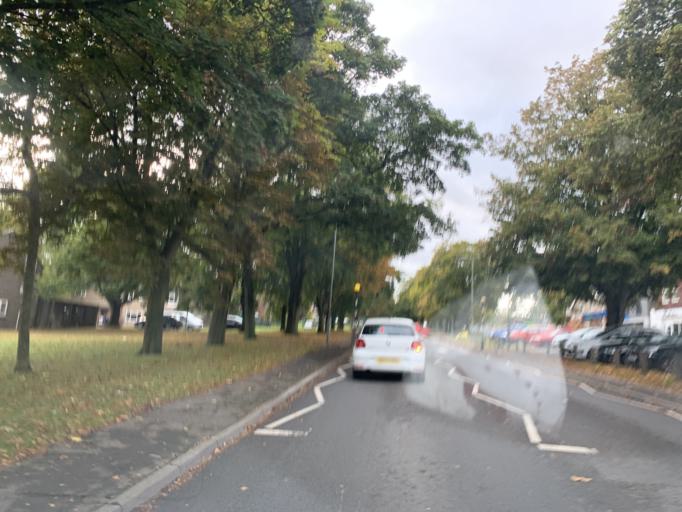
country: GB
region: England
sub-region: Wiltshire
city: Amesbury
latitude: 51.1974
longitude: -1.8151
